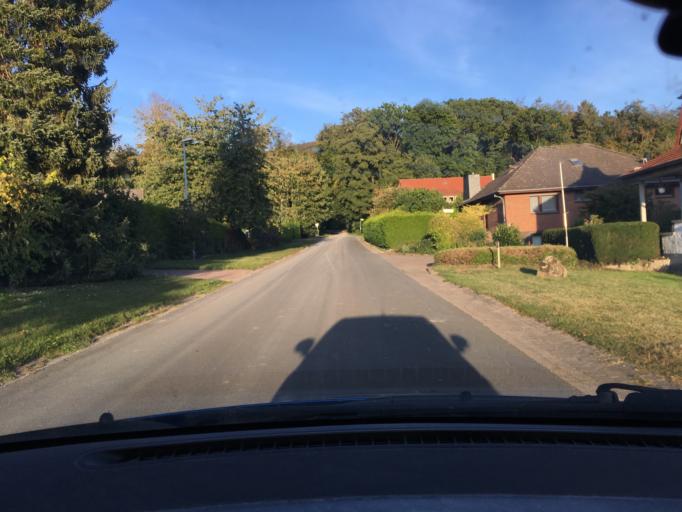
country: DE
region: Lower Saxony
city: Lauenau
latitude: 52.2862
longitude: 9.3964
